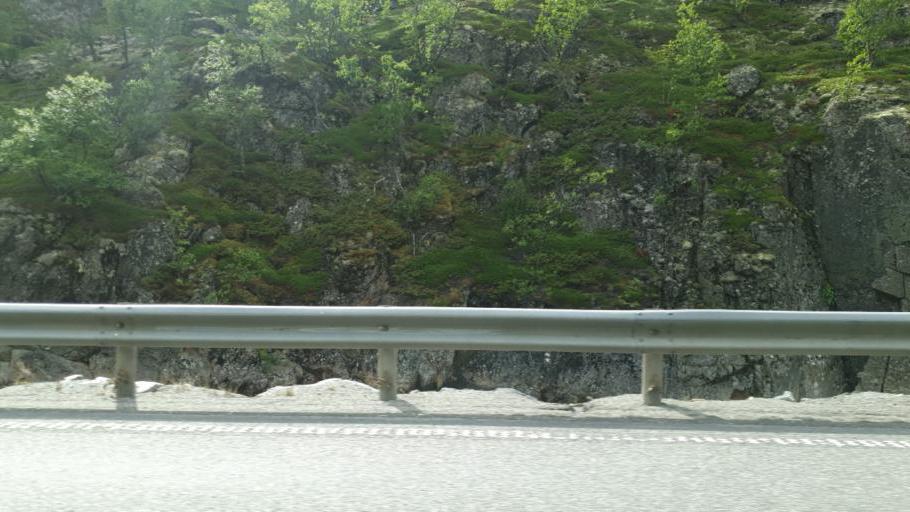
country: NO
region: Sor-Trondelag
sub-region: Oppdal
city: Oppdal
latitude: 62.3548
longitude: 9.6321
